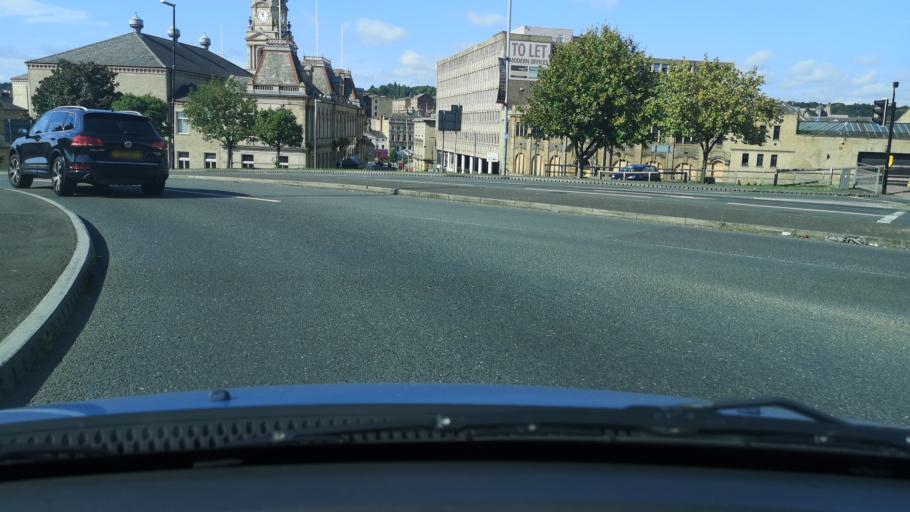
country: GB
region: England
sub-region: Kirklees
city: Dewsbury
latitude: 53.6916
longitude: -1.6250
